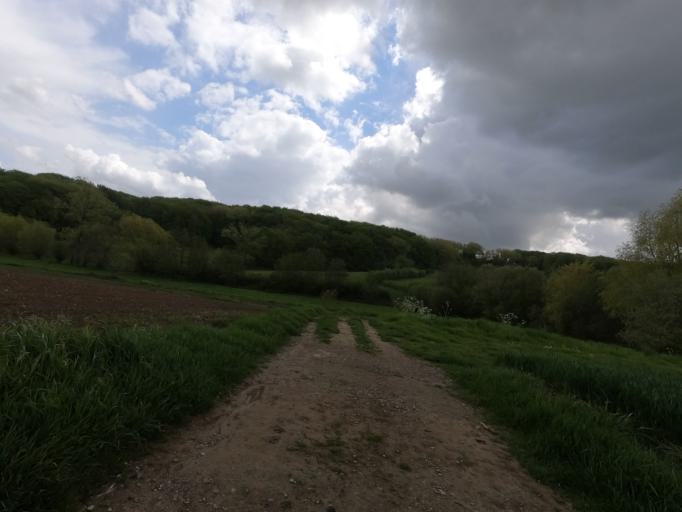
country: BE
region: Flanders
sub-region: Provincie Oost-Vlaanderen
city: Ronse
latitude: 50.7740
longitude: 3.5584
